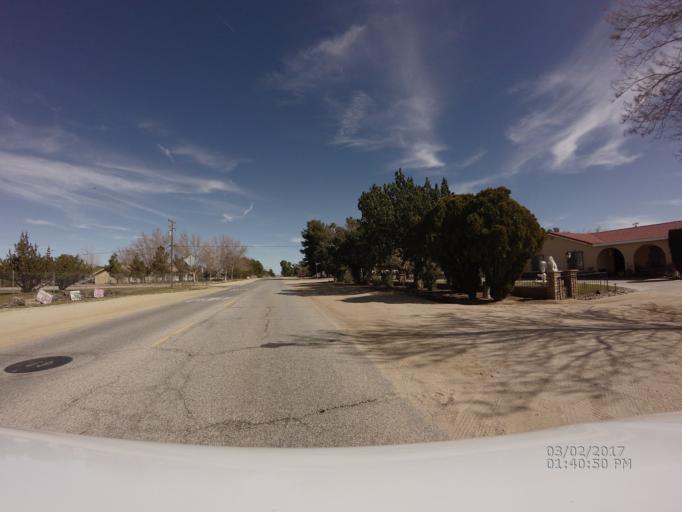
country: US
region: California
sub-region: Los Angeles County
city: Desert View Highlands
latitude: 34.6091
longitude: -118.1638
